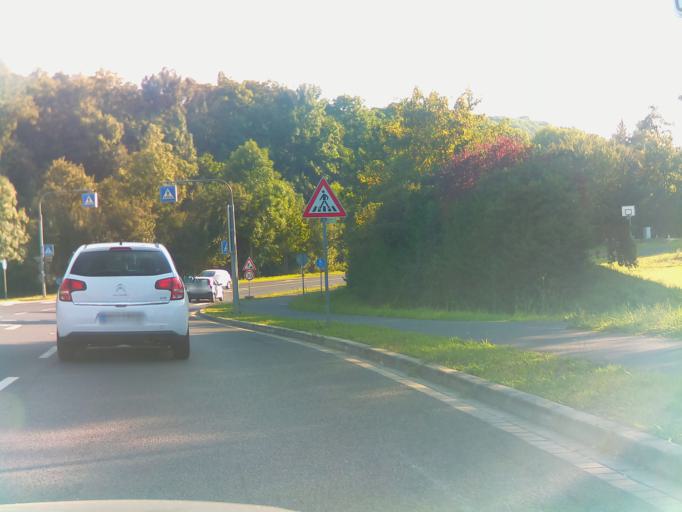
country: DE
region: Bavaria
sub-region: Regierungsbezirk Unterfranken
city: Ochsenfurt
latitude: 49.6693
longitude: 10.0462
